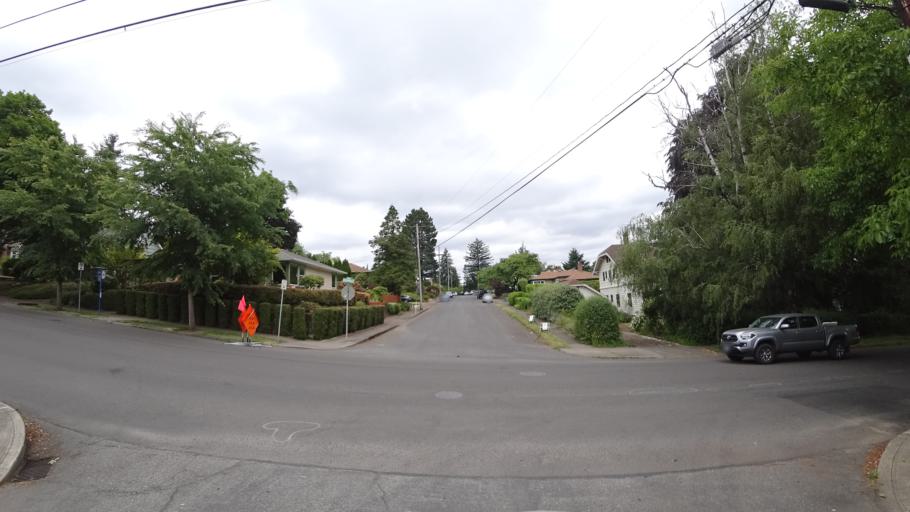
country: US
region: Oregon
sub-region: Multnomah County
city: Lents
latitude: 45.5162
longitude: -122.5876
